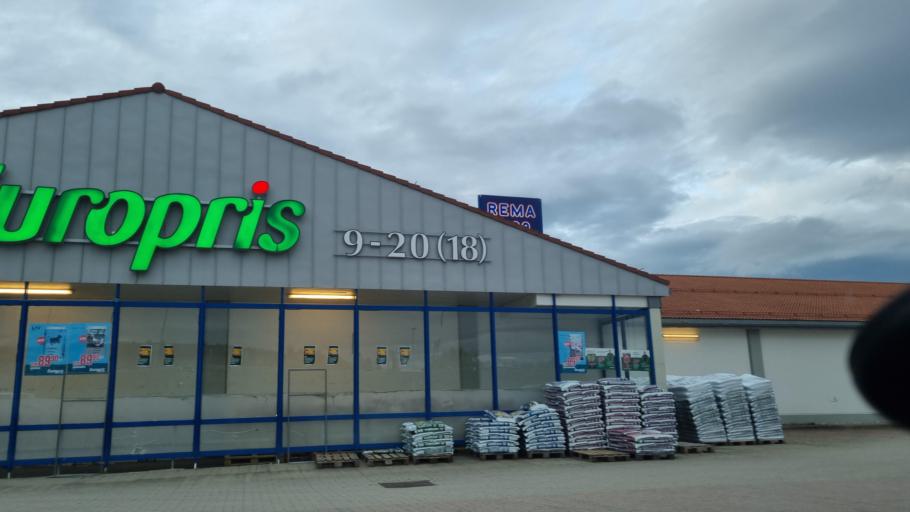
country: NO
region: Sor-Trondelag
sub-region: Malvik
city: Hommelvik
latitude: 63.4204
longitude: 10.7568
